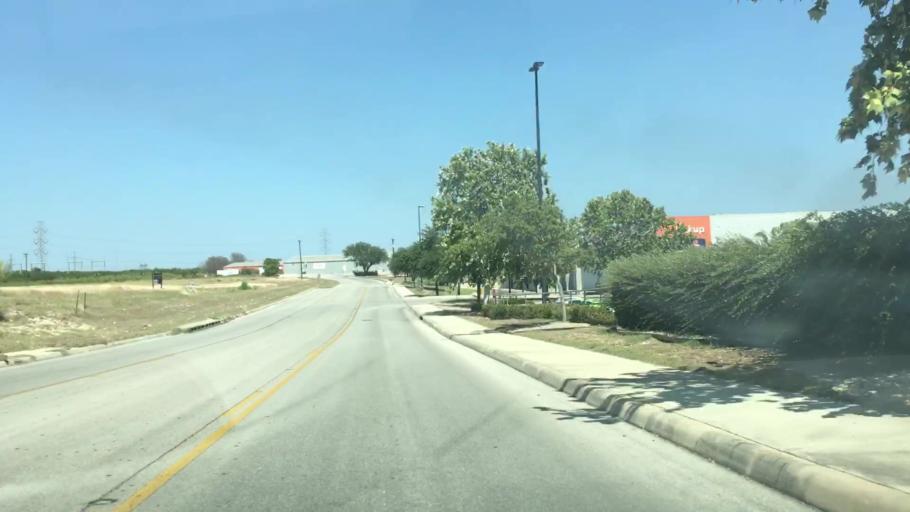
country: US
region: Texas
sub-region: Bexar County
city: Selma
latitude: 29.6044
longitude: -98.2769
